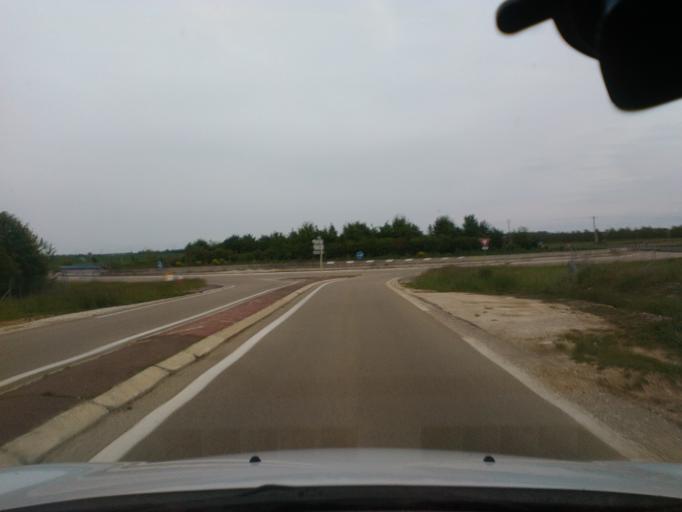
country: FR
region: Champagne-Ardenne
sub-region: Departement de la Haute-Marne
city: Chaumont
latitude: 48.1286
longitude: 5.1057
